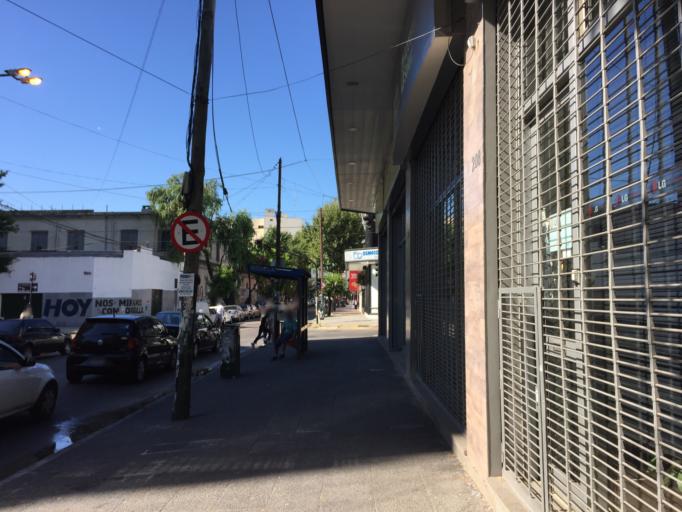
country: AR
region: Buenos Aires
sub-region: Partido de Lomas de Zamora
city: Lomas de Zamora
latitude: -34.7579
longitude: -58.4006
